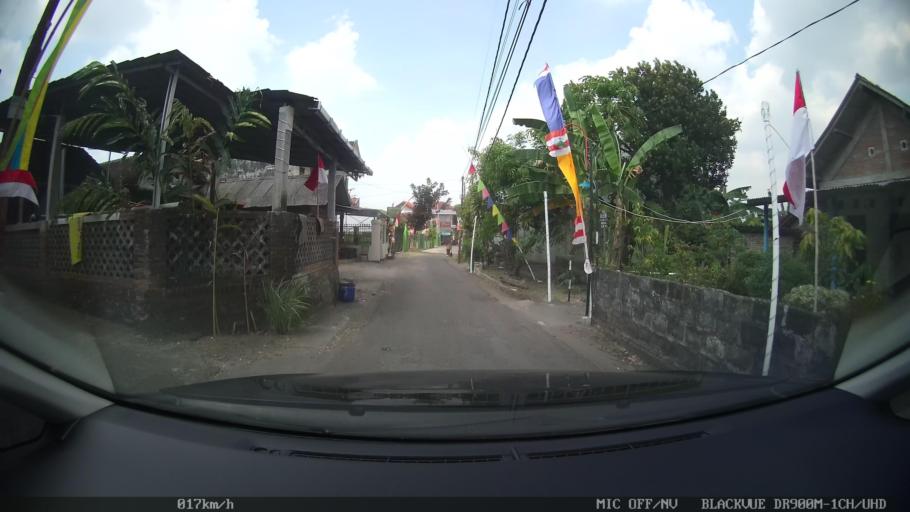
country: ID
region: Daerah Istimewa Yogyakarta
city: Depok
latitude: -7.8060
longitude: 110.4074
